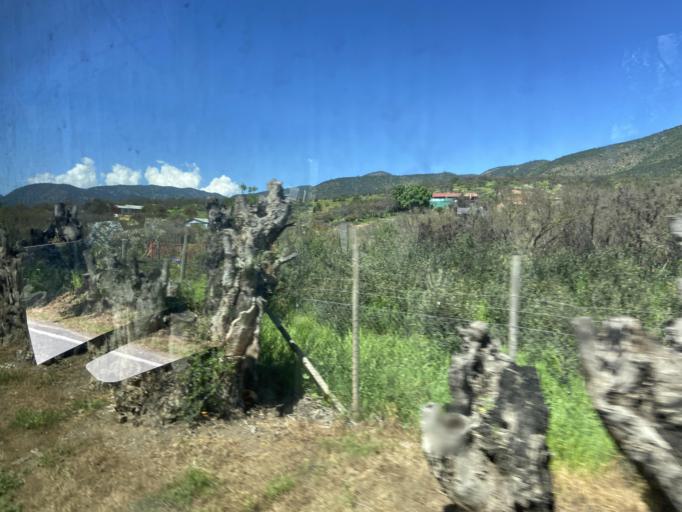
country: CL
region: Valparaiso
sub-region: Provincia de Marga Marga
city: Villa Alemana
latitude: -33.1652
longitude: -71.3167
